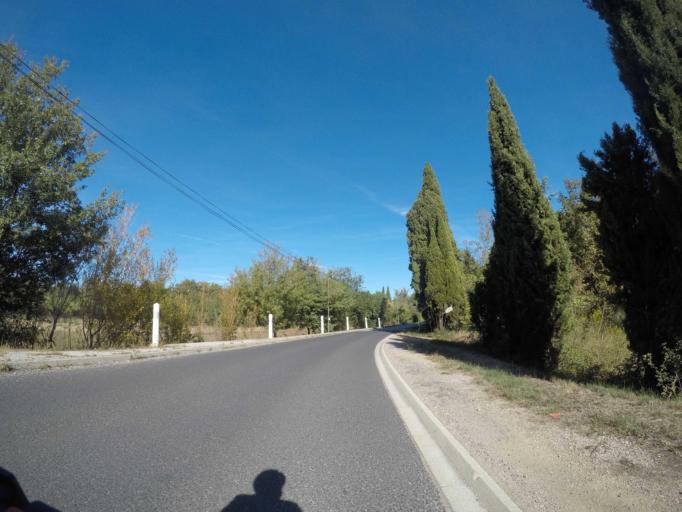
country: FR
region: Languedoc-Roussillon
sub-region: Departement des Pyrenees-Orientales
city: Le Soler
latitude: 42.6714
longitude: 2.7893
